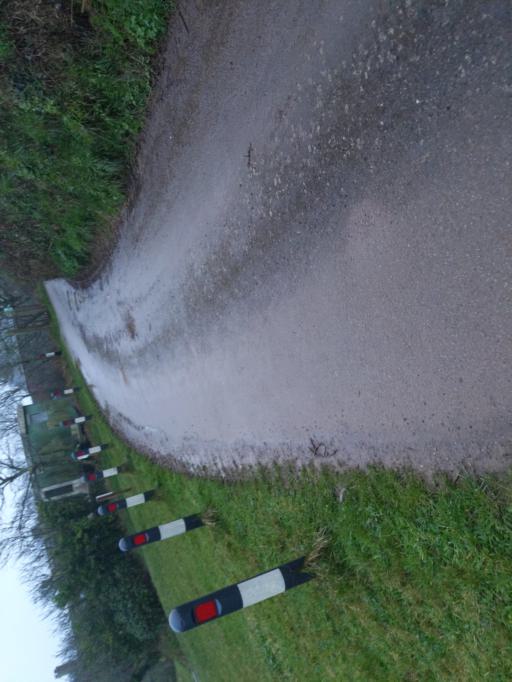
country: GB
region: England
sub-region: Cornwall
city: Torpoint
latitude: 50.3363
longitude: -4.2178
